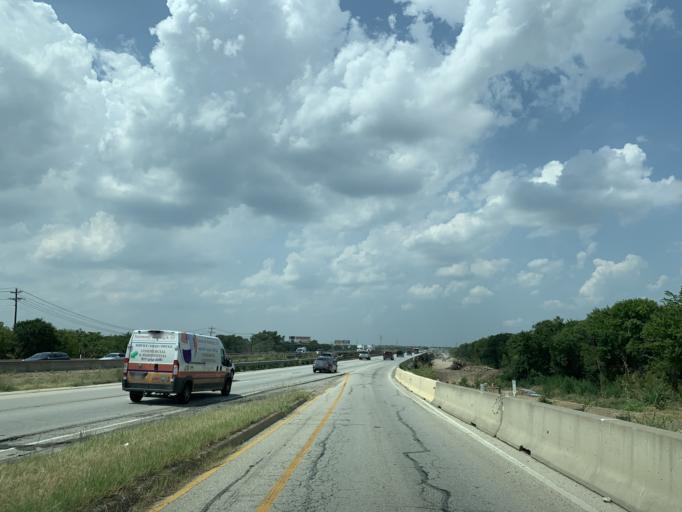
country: US
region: Texas
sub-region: Tarrant County
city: Richland Hills
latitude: 32.7799
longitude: -97.2124
